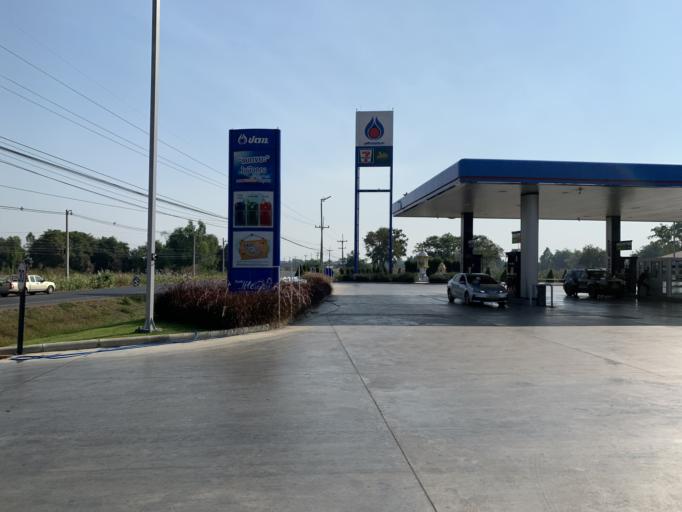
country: TH
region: Nakhon Sawan
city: Chumsaeng
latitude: 15.7876
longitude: 100.2583
